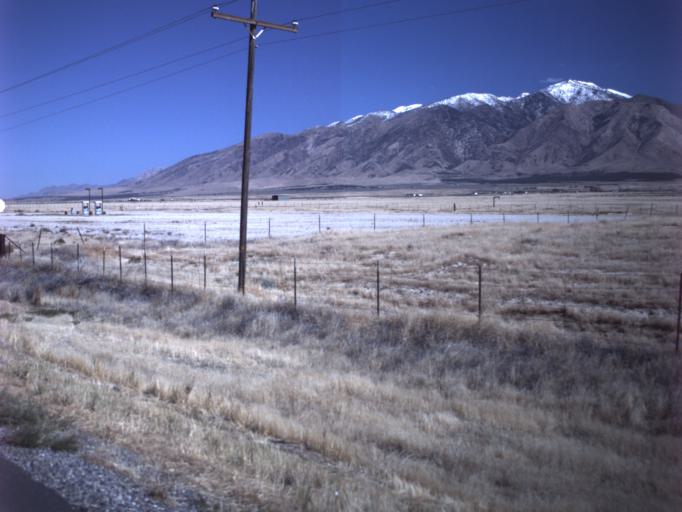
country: US
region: Utah
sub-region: Tooele County
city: Grantsville
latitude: 40.3788
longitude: -112.7468
